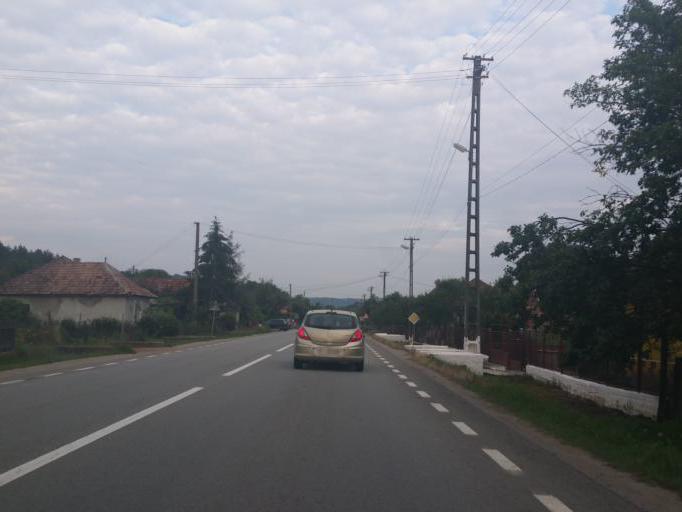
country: RO
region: Salaj
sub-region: Comuna Sanmihaiu Almasului
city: Sanmihaiu Almasului
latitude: 46.9593
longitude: 23.3309
